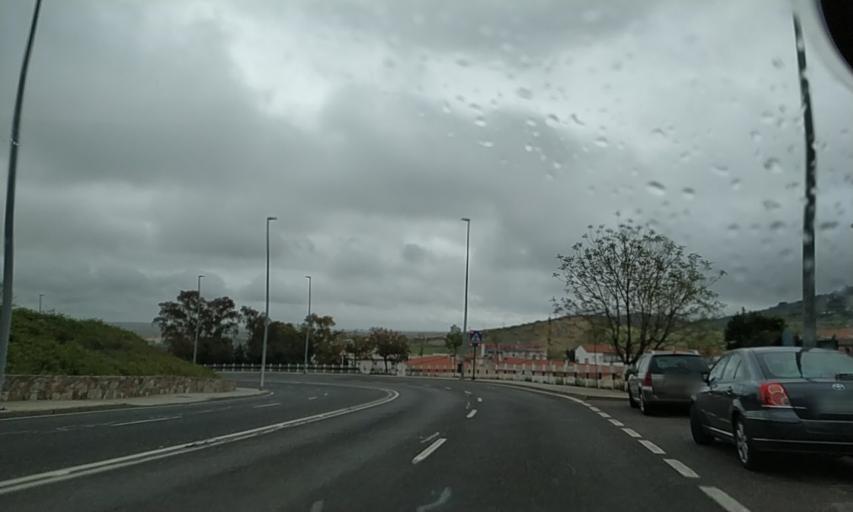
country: ES
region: Extremadura
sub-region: Provincia de Caceres
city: Caceres
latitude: 39.4800
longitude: -6.3714
